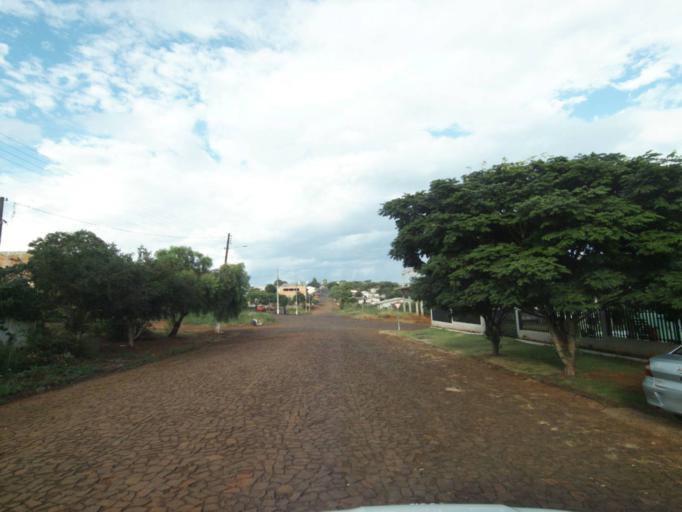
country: BR
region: Parana
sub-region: Laranjeiras Do Sul
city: Laranjeiras do Sul
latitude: -25.4942
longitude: -52.5306
